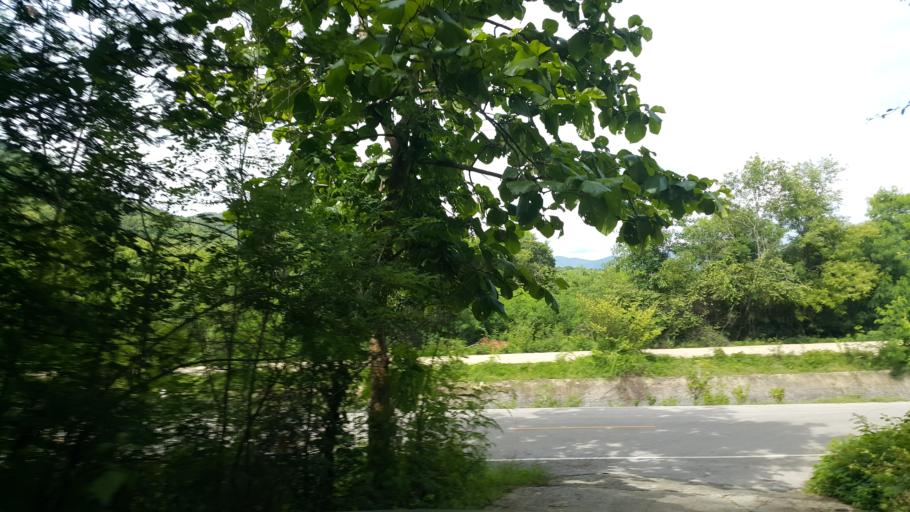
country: TH
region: Chiang Mai
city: Mae On
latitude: 18.7454
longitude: 99.1998
